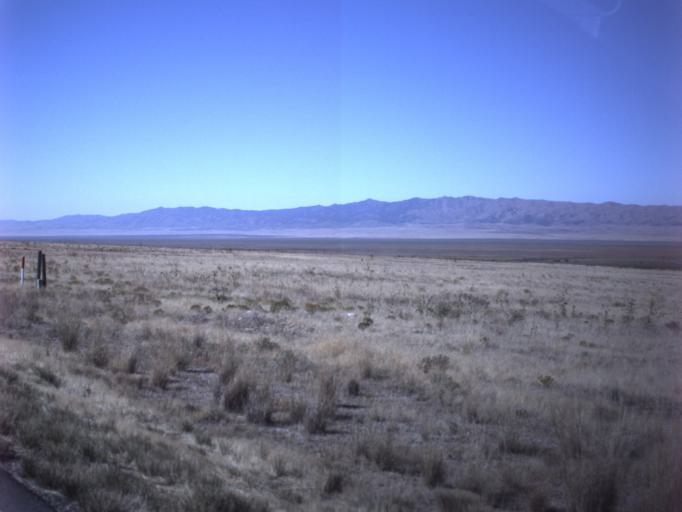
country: US
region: Utah
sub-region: Tooele County
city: Grantsville
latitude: 40.5944
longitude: -112.7180
